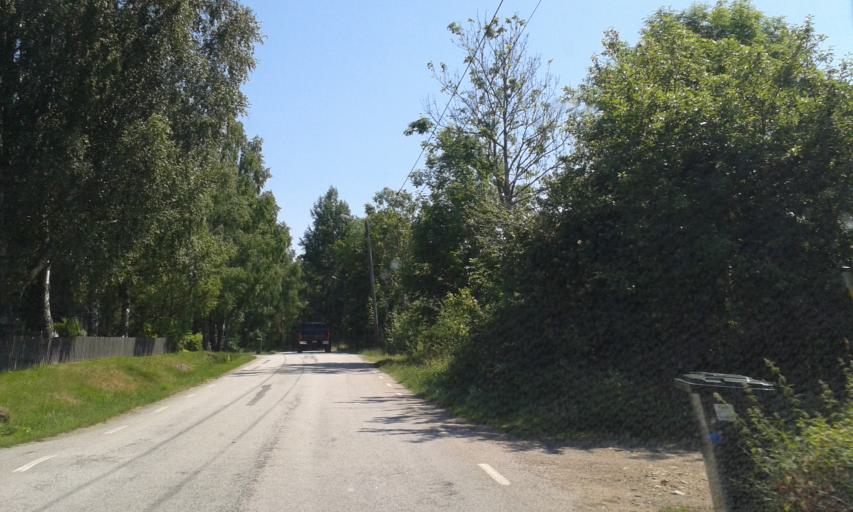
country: SE
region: Blekinge
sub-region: Karlskrona Kommun
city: Rodeby
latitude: 56.2436
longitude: 15.5602
